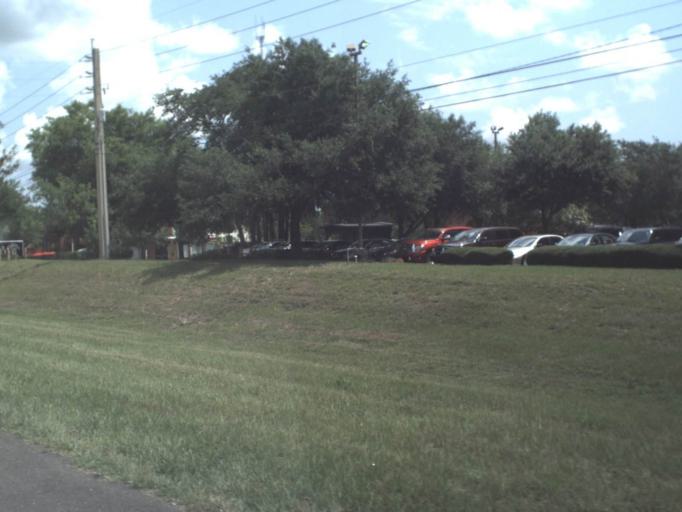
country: US
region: Florida
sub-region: Duval County
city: Jacksonville
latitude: 30.2627
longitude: -81.5571
